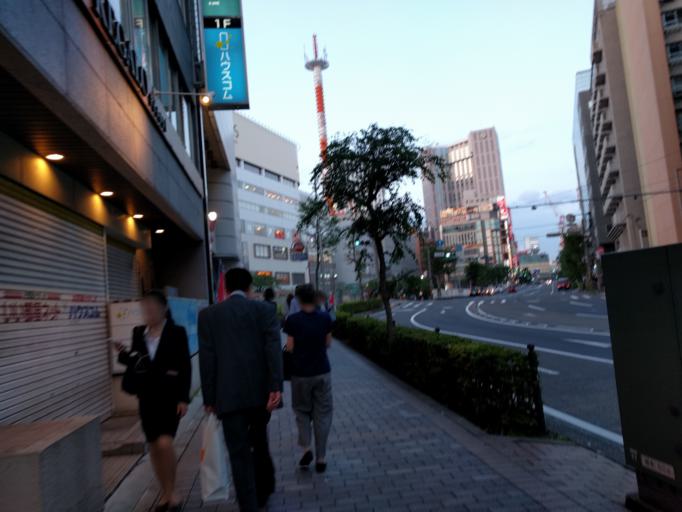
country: JP
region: Kanagawa
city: Yokohama
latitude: 35.4648
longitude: 139.6167
